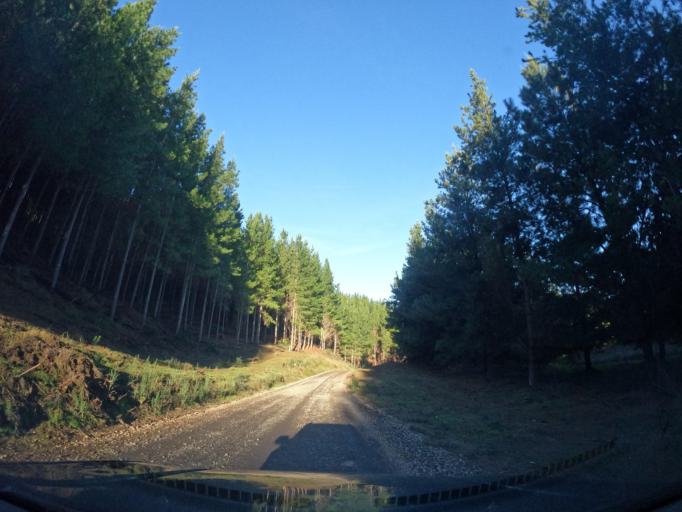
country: CL
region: Biobio
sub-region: Provincia de Concepcion
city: Chiguayante
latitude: -37.0882
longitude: -72.9025
